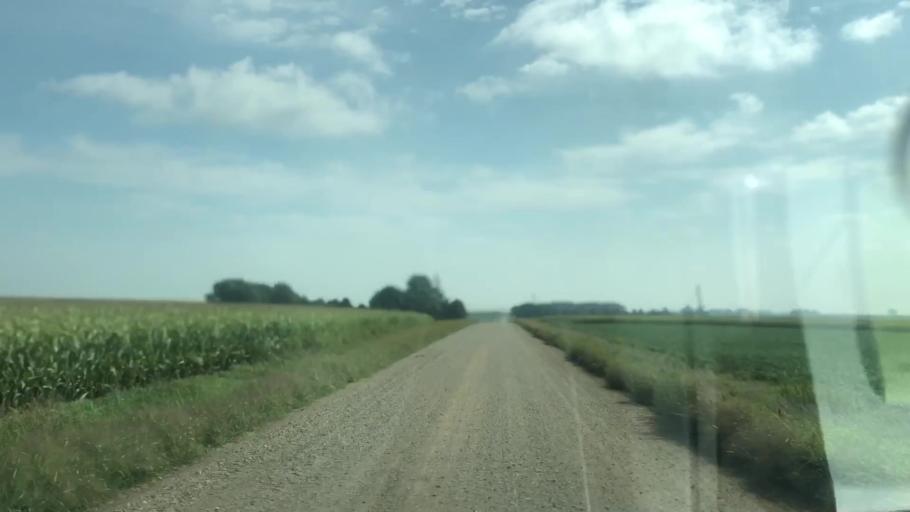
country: US
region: Iowa
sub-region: Lyon County
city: George
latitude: 43.2153
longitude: -95.9926
